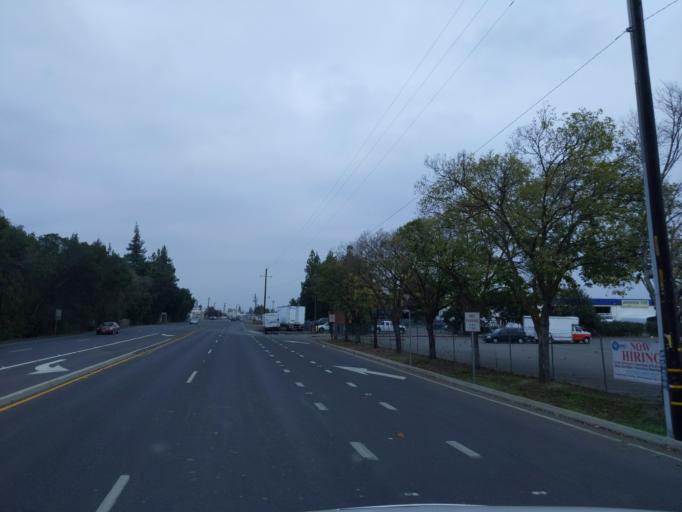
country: US
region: California
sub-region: San Joaquin County
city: August
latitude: 37.9919
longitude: -121.2664
